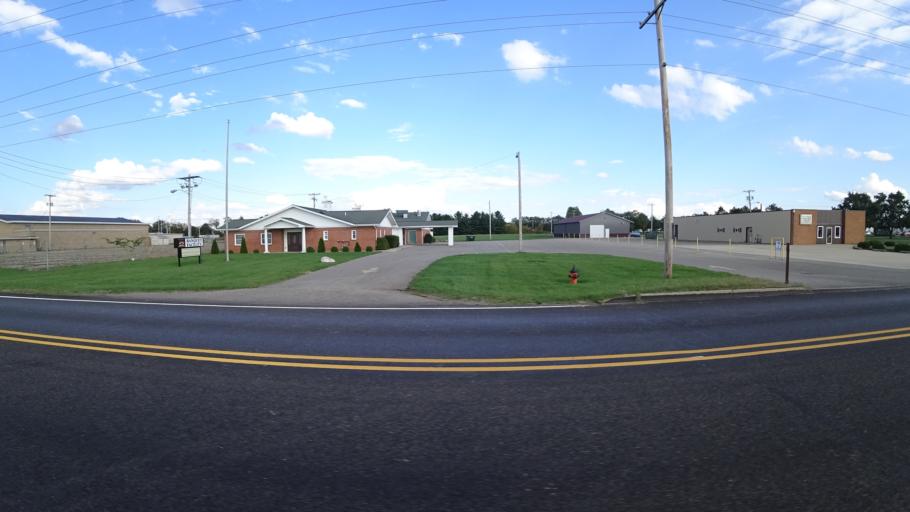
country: US
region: Michigan
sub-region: Saint Joseph County
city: Sturgis
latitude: 41.8132
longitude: -85.4285
